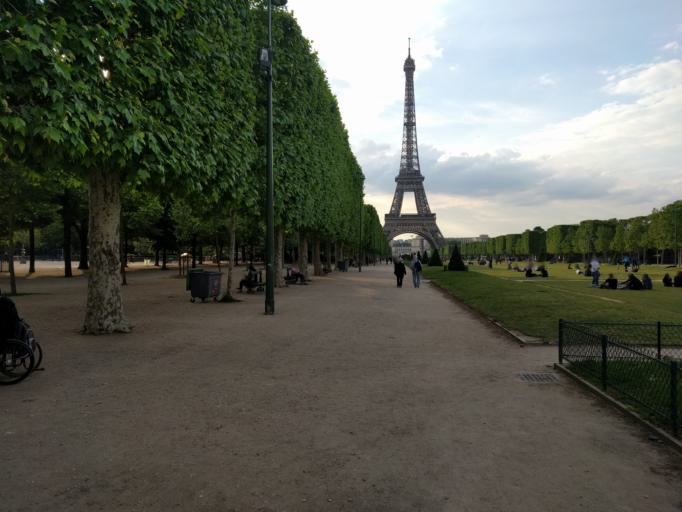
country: FR
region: Ile-de-France
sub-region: Departement des Hauts-de-Seine
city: Vanves
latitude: 48.8534
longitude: 2.3017
